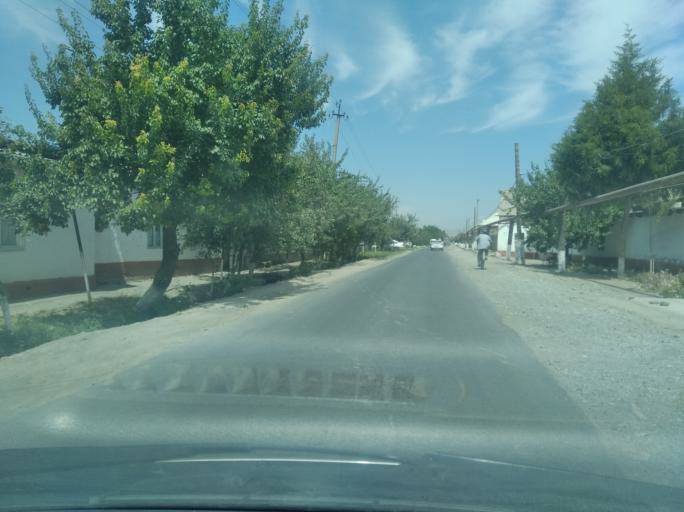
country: KG
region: Osh
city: Aravan
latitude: 40.6079
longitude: 72.4583
